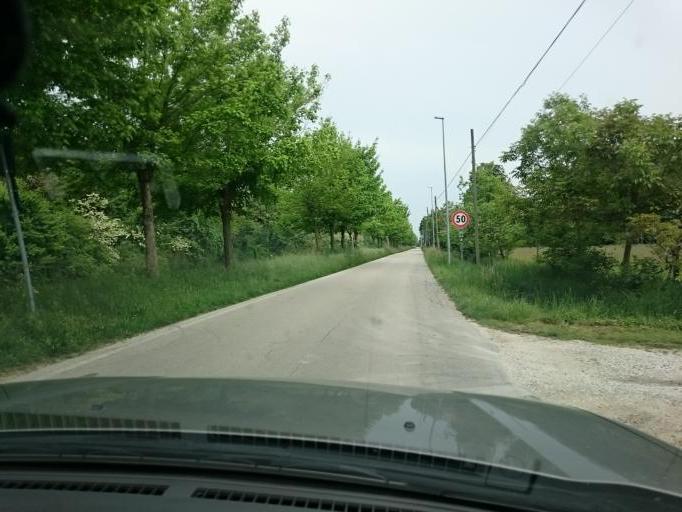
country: IT
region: Veneto
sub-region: Provincia di Venezia
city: Fiesso
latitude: 45.4130
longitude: 12.0434
